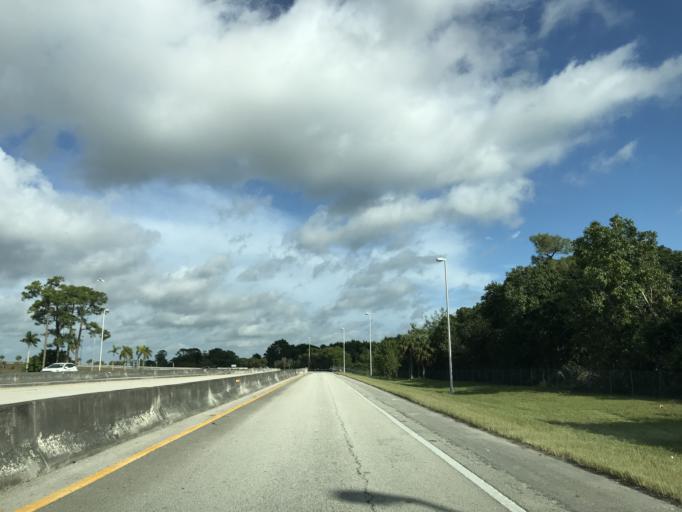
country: US
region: Florida
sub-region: Palm Beach County
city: Boca Del Mar
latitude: 26.3720
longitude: -80.1689
